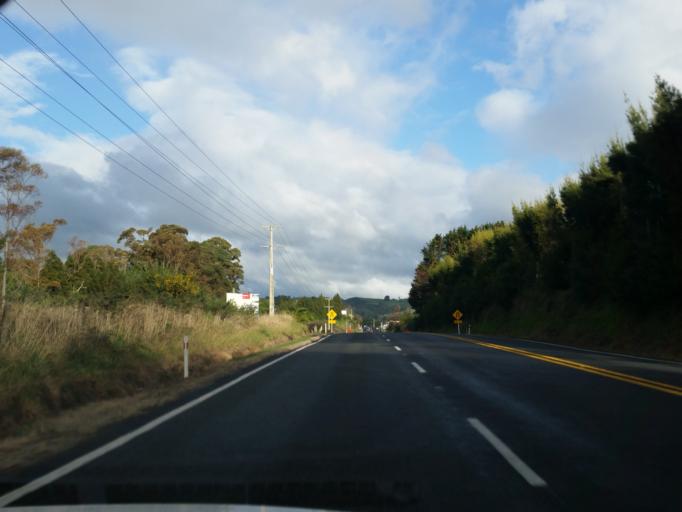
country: NZ
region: Bay of Plenty
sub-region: Tauranga City
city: Tauranga
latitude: -37.6747
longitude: 176.0231
